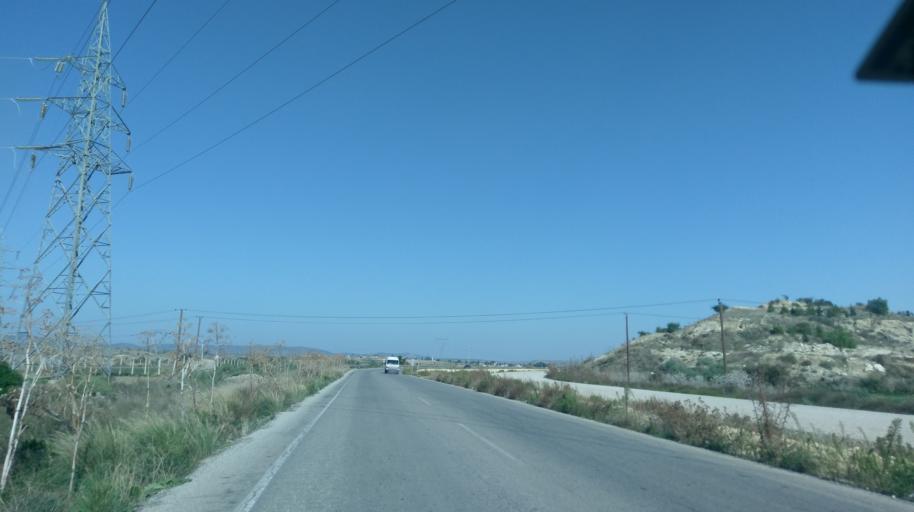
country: CY
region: Ammochostos
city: Trikomo
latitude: 35.3454
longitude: 33.9859
